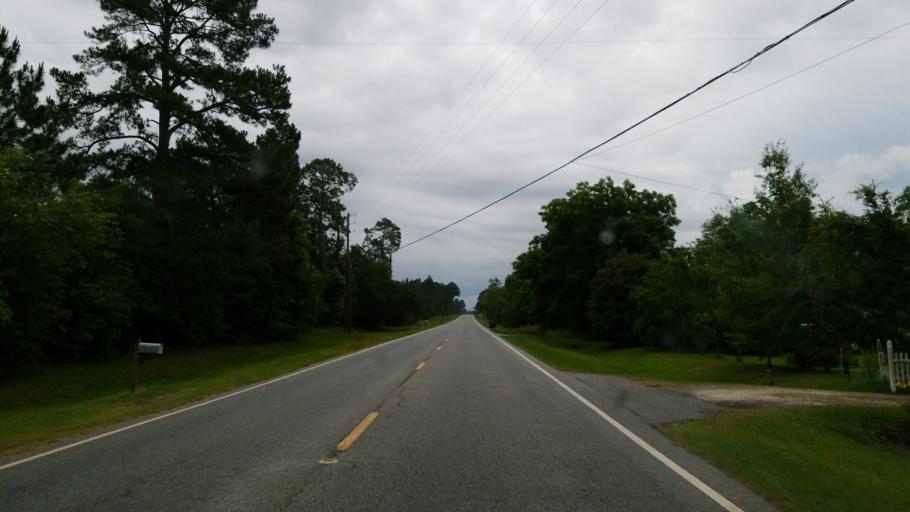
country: US
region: Georgia
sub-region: Berrien County
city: Ray City
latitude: 31.0652
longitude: -83.1667
